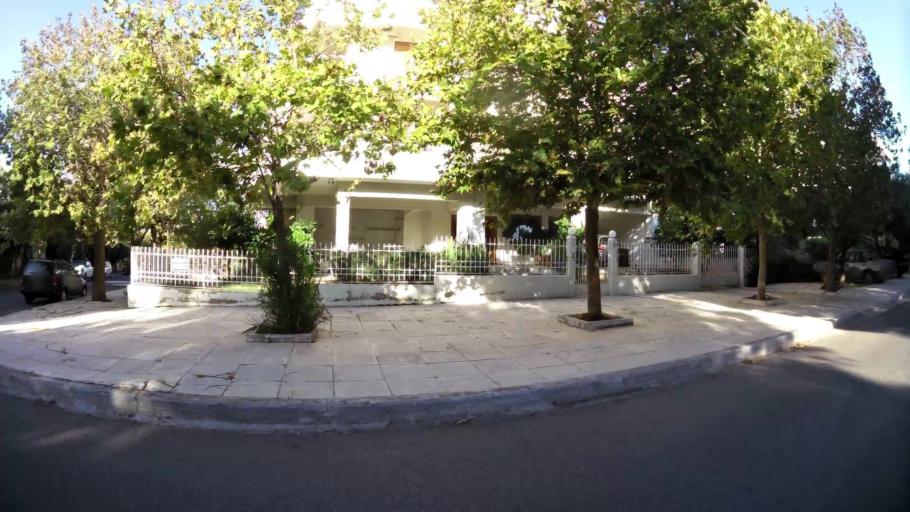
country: GR
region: Attica
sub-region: Nomarchia Athinas
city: Glyfada
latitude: 37.8787
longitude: 23.7509
